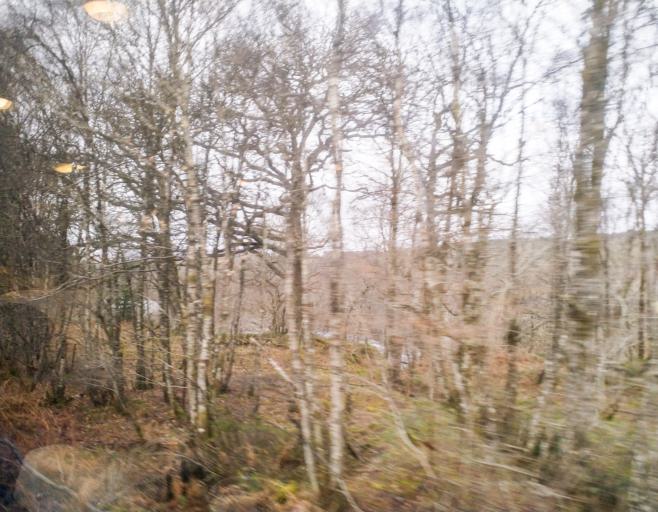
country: GB
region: Scotland
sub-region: Highland
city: Spean Bridge
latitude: 56.8926
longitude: -4.8998
